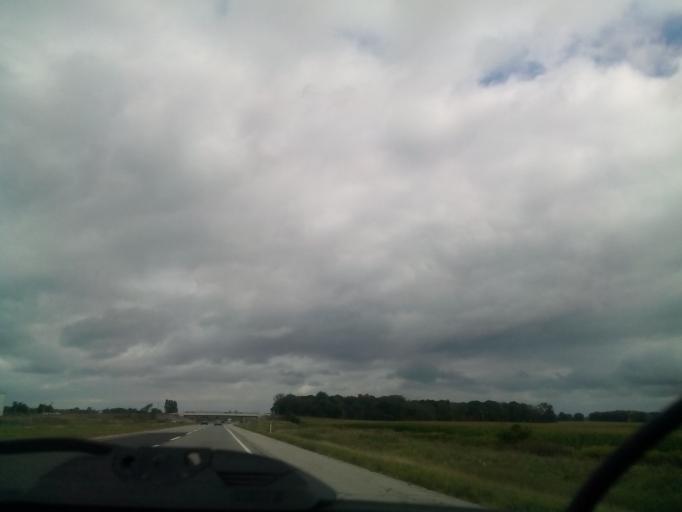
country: US
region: Indiana
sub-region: Steuben County
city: Fremont
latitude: 41.6890
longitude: -84.8936
